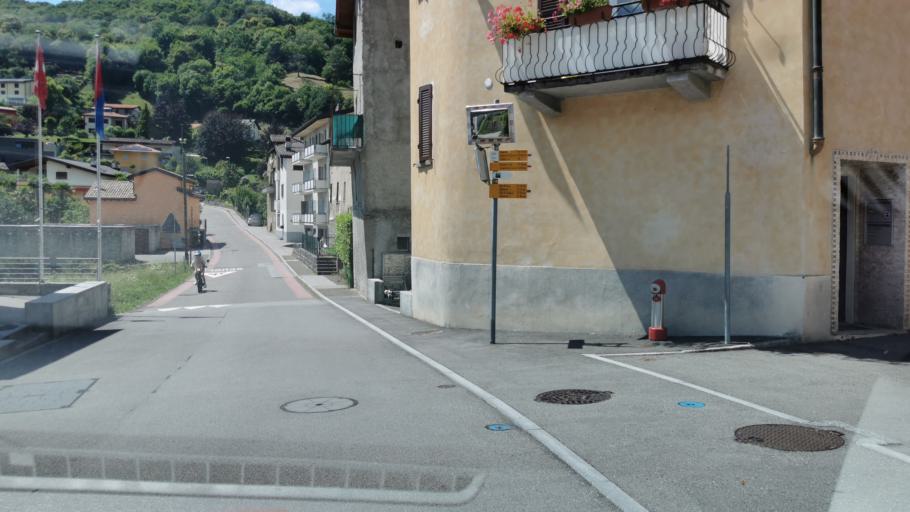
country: IT
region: Lombardy
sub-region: Provincia di Como
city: Campione
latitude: 45.9589
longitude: 8.9873
